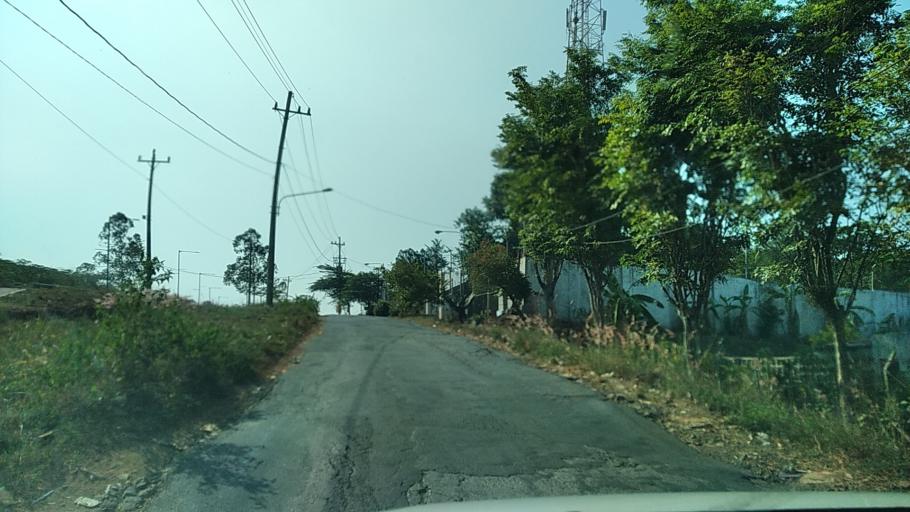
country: ID
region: Central Java
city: Semarang
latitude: -7.0420
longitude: 110.3348
